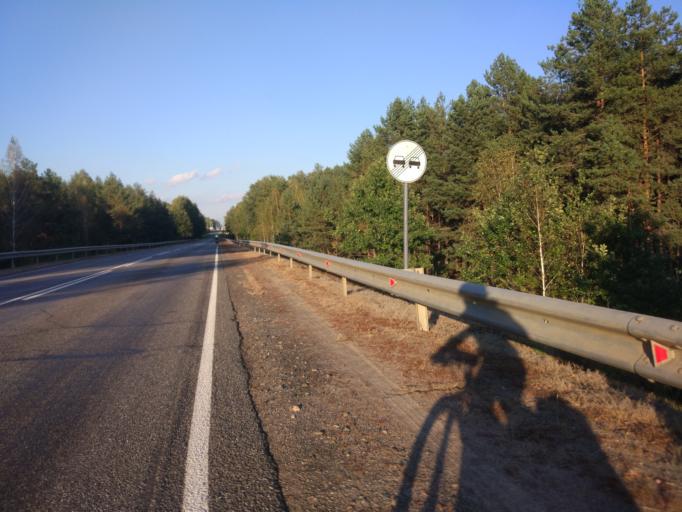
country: RU
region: Brjansk
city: Zamishevo
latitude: 52.5016
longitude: 31.9835
